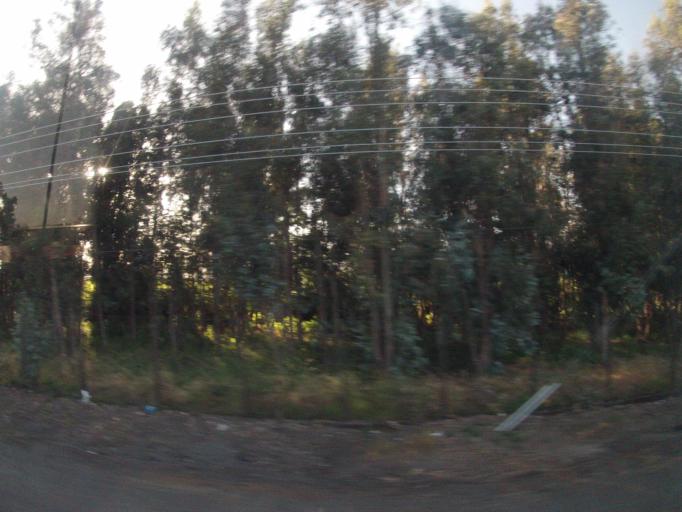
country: CL
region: O'Higgins
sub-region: Provincia de Colchagua
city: Chimbarongo
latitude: -34.7227
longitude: -71.0344
